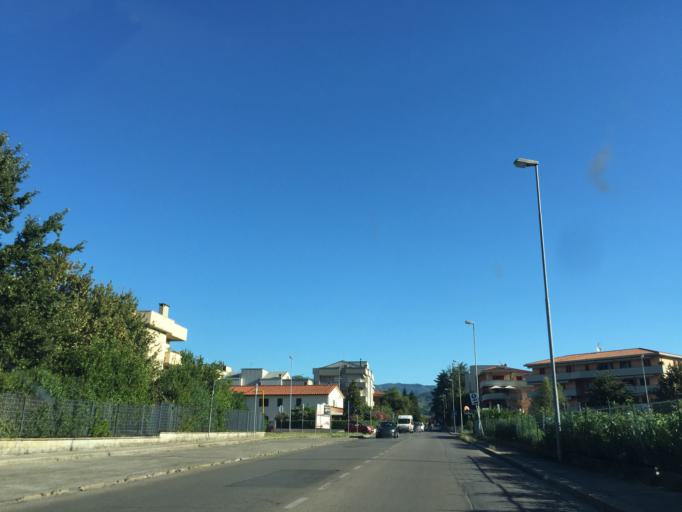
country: IT
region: Tuscany
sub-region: Provincia di Pistoia
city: Pistoia
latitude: 43.9349
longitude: 10.8974
